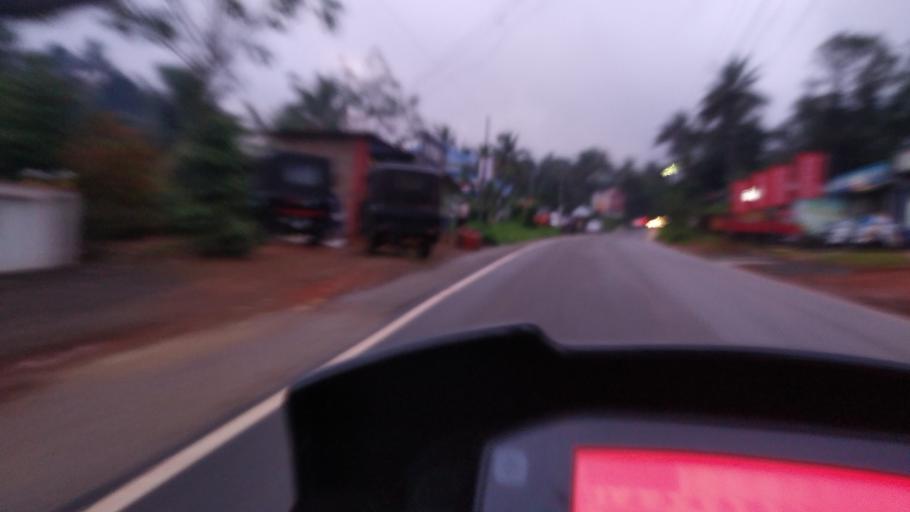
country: IN
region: Kerala
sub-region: Idukki
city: Munnar
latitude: 9.9589
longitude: 77.0935
